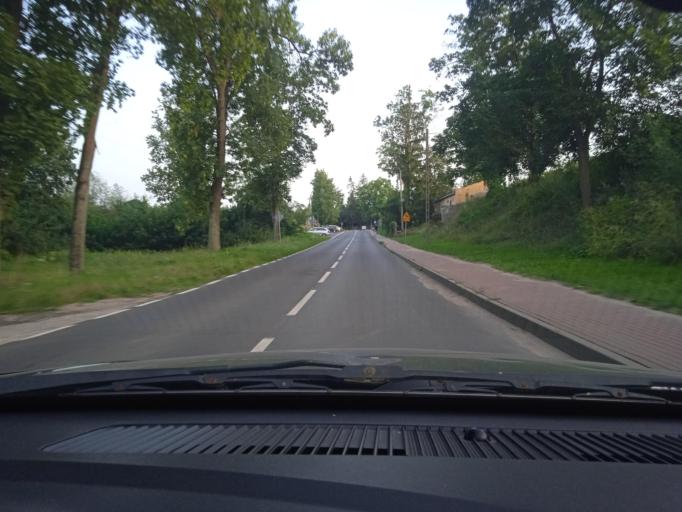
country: PL
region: Masovian Voivodeship
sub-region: Powiat nowodworski
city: Pomiechowek
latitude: 52.4762
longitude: 20.7252
